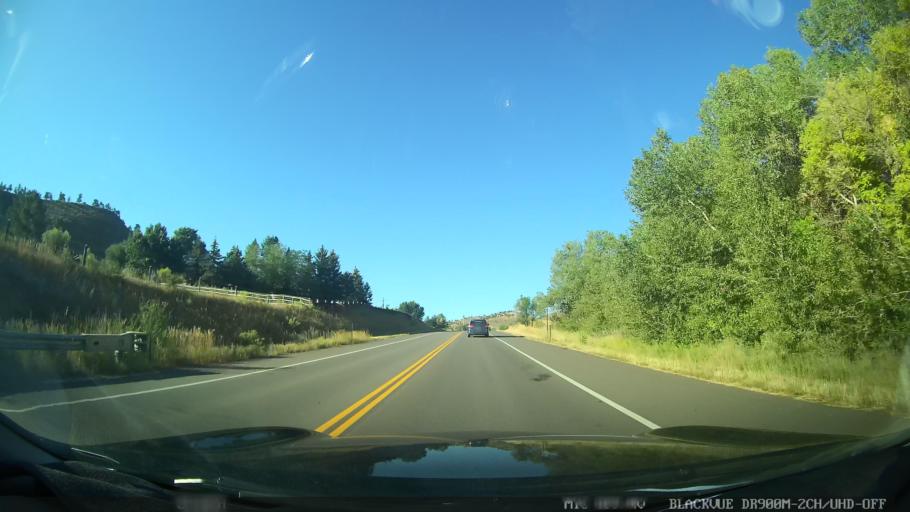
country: US
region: Colorado
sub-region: Larimer County
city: Loveland
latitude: 40.4149
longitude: -105.1954
